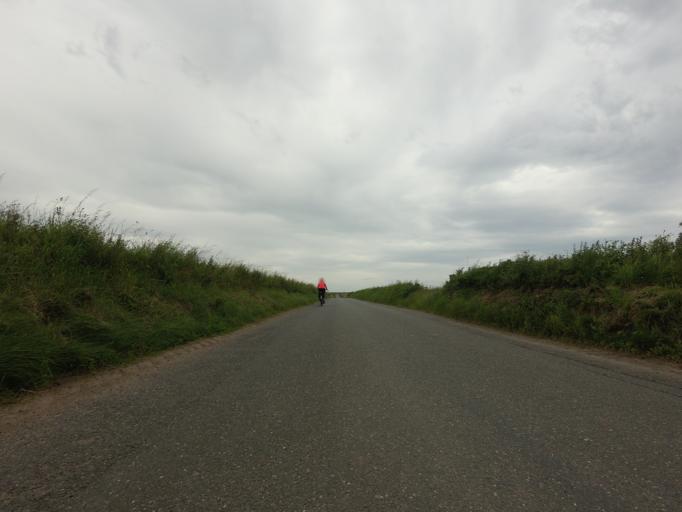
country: GB
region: Scotland
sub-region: Aberdeenshire
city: Whitehills
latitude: 57.6704
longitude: -2.6013
